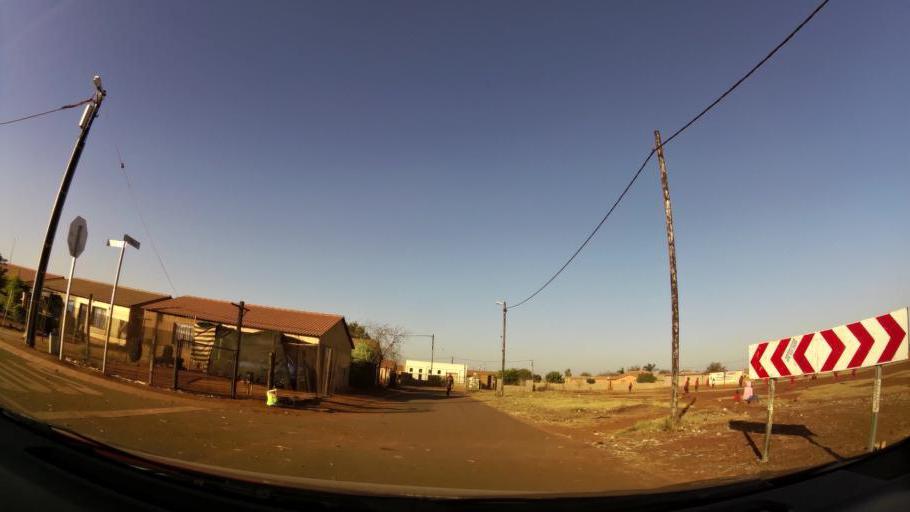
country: ZA
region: Gauteng
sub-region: City of Tshwane Metropolitan Municipality
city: Mabopane
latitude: -25.5968
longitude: 28.1079
